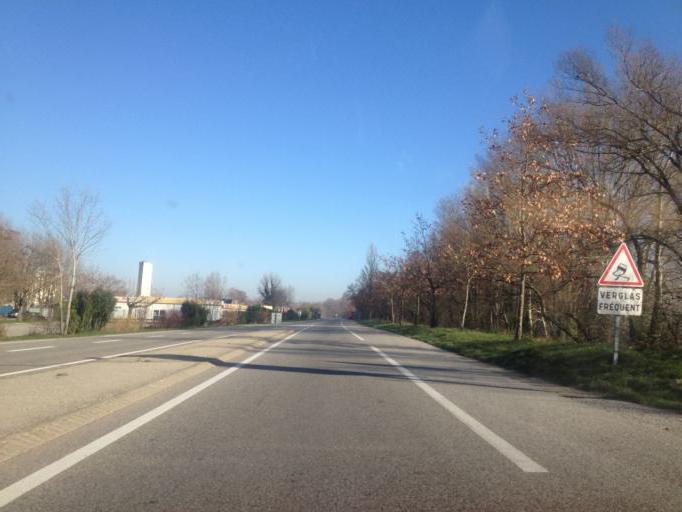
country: FR
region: Rhone-Alpes
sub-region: Departement de l'Ardeche
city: La Voulte-sur-Rhone
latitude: 44.8025
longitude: 4.7860
